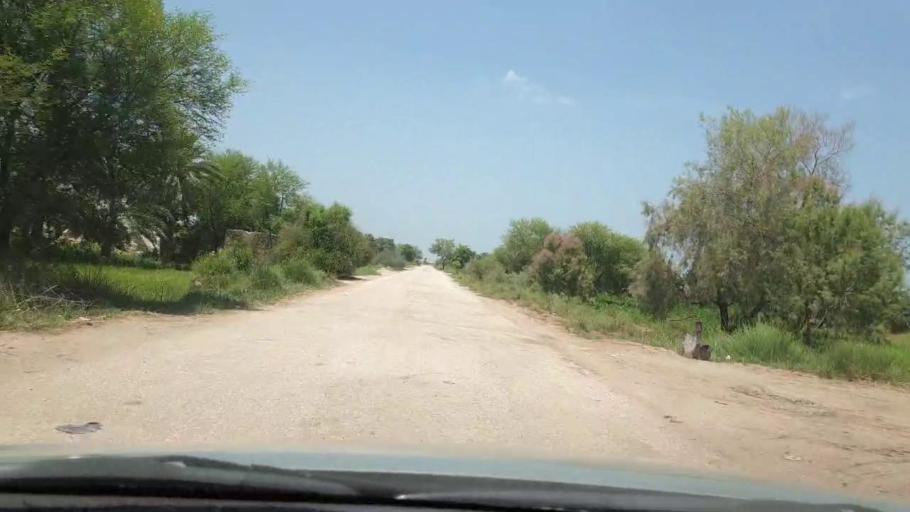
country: PK
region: Sindh
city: Pano Aqil
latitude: 27.7097
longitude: 69.2162
